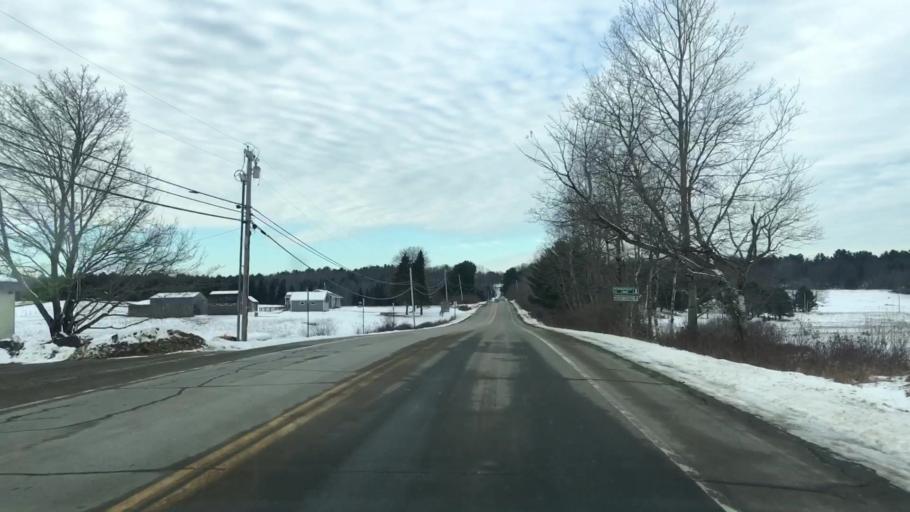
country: US
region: Maine
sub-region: Lincoln County
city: Whitefield
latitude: 44.2235
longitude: -69.6032
